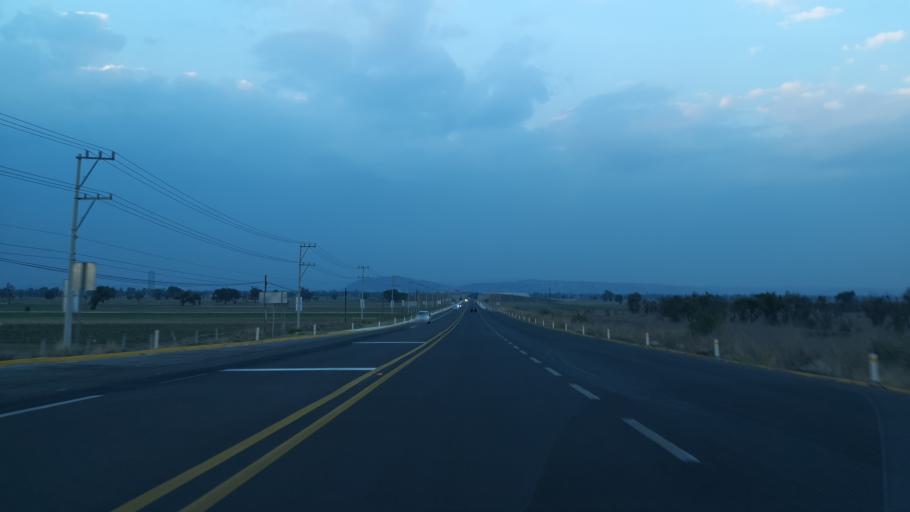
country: MX
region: Puebla
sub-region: Huejotzingo
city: Los Encinos
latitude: 19.1802
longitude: -98.3727
